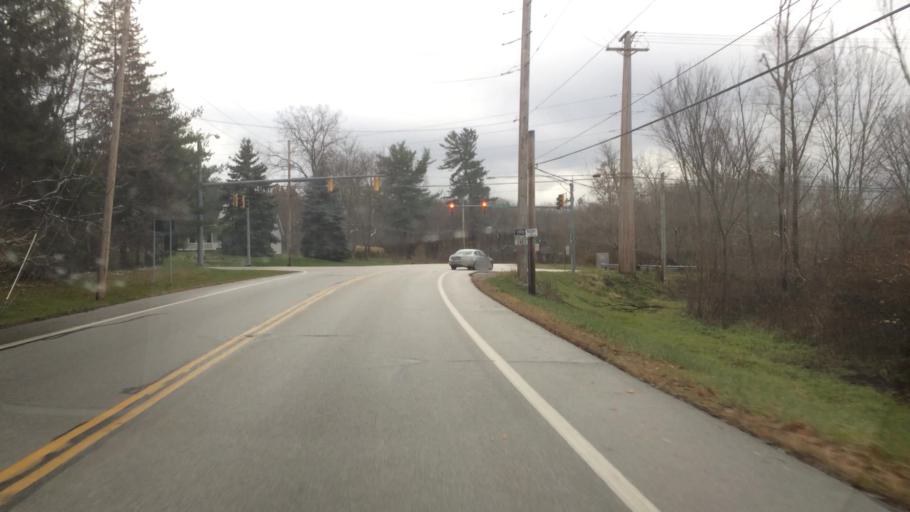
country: US
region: Ohio
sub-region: Summit County
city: Hudson
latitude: 41.2036
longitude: -81.4112
